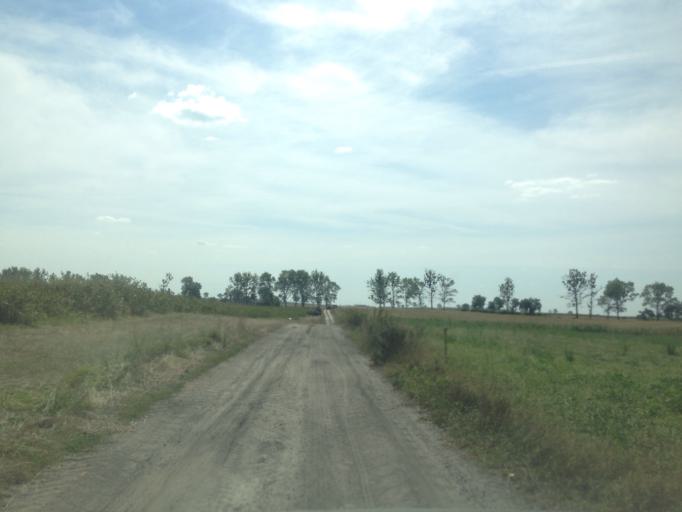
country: PL
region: Kujawsko-Pomorskie
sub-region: Powiat brodnicki
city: Gorzno
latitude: 53.2130
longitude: 19.6272
